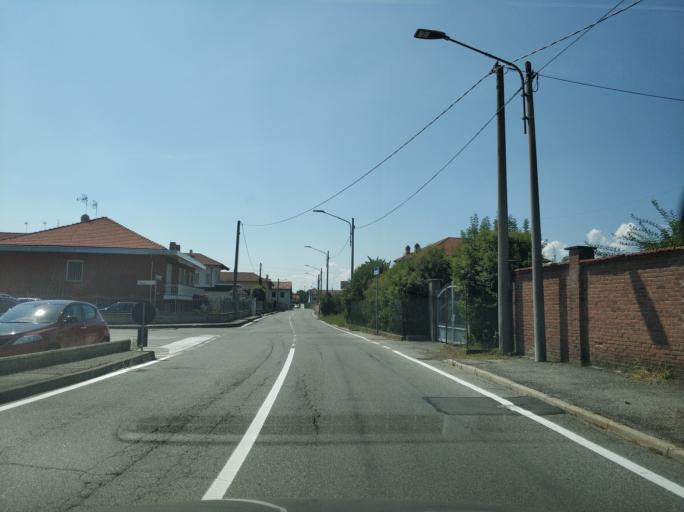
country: IT
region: Piedmont
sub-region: Provincia di Torino
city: San Maurizio
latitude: 45.2121
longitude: 7.6230
